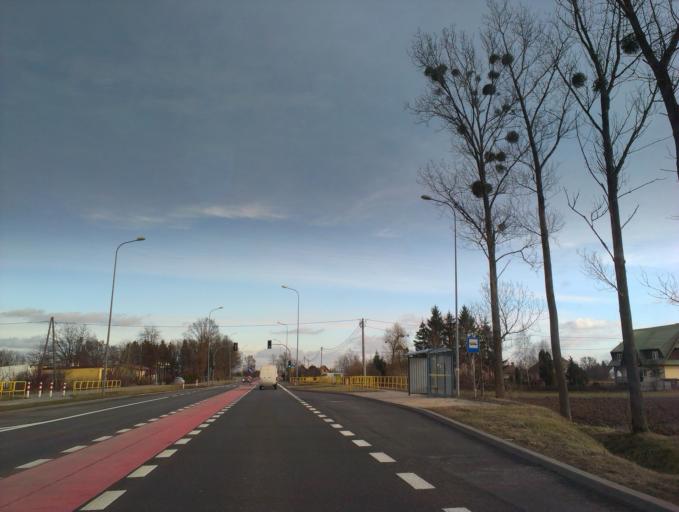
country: PL
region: Kujawsko-Pomorskie
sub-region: Powiat torunski
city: Czernikowo
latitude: 52.9333
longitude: 19.0119
